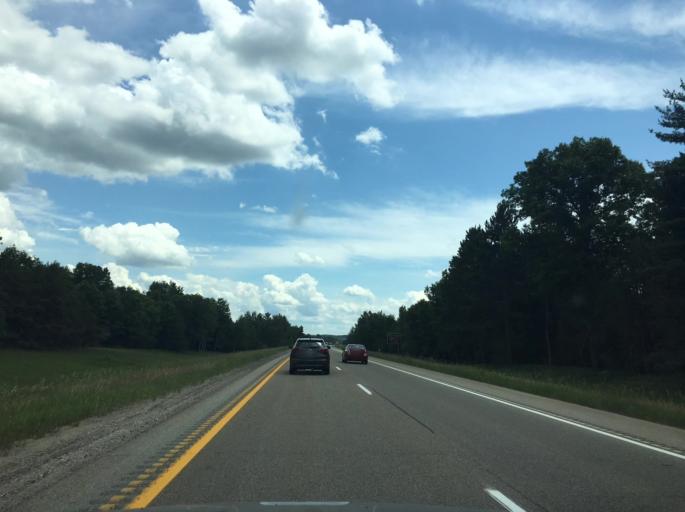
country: US
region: Michigan
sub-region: Roscommon County
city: Roscommon
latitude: 44.5243
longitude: -84.6721
